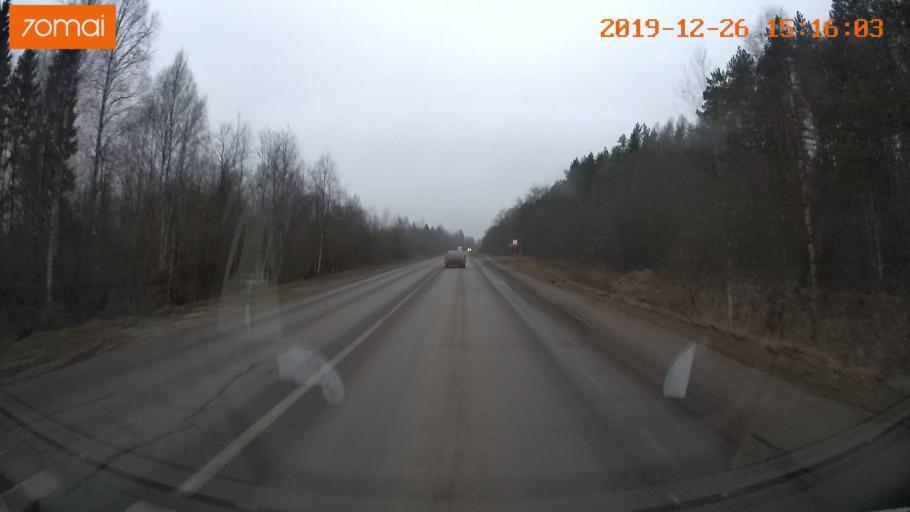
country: RU
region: Jaroslavl
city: Rybinsk
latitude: 58.0905
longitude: 38.8710
